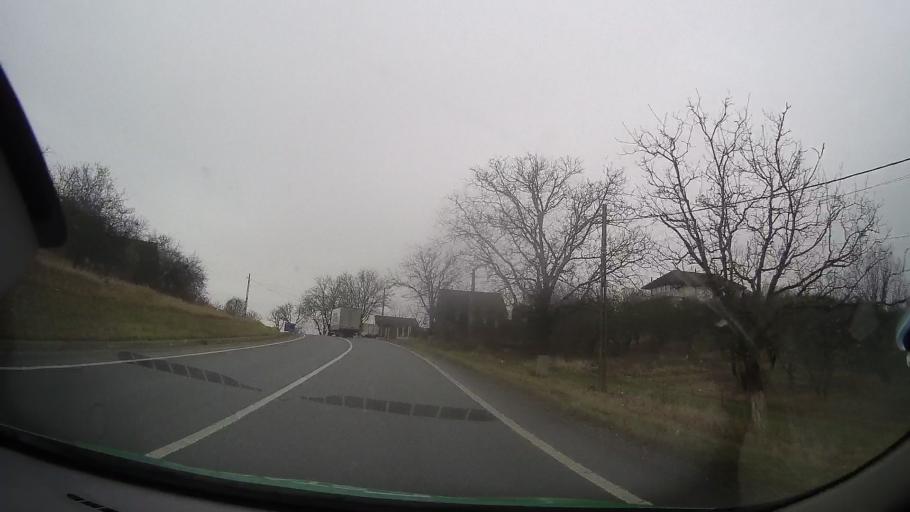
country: RO
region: Mures
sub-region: Comuna Breaza
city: Breaza
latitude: 46.7648
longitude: 24.6592
